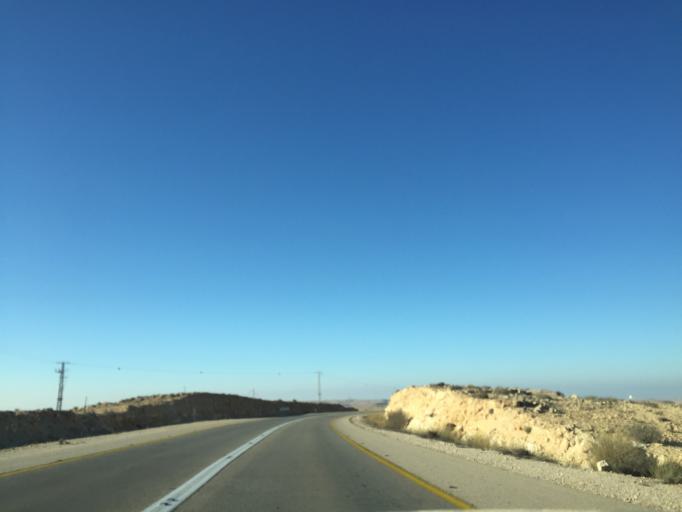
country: IL
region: Southern District
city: Midreshet Ben-Gurion
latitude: 30.7315
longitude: 34.7713
